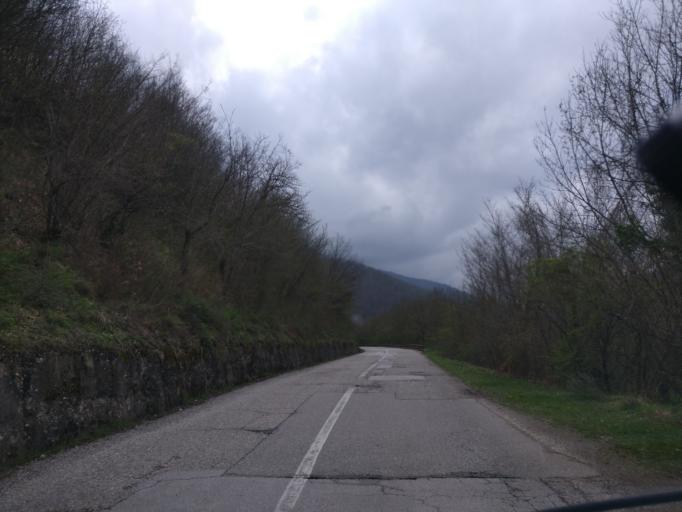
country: BA
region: Republika Srpska
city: Foca
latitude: 43.4567
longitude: 18.7493
